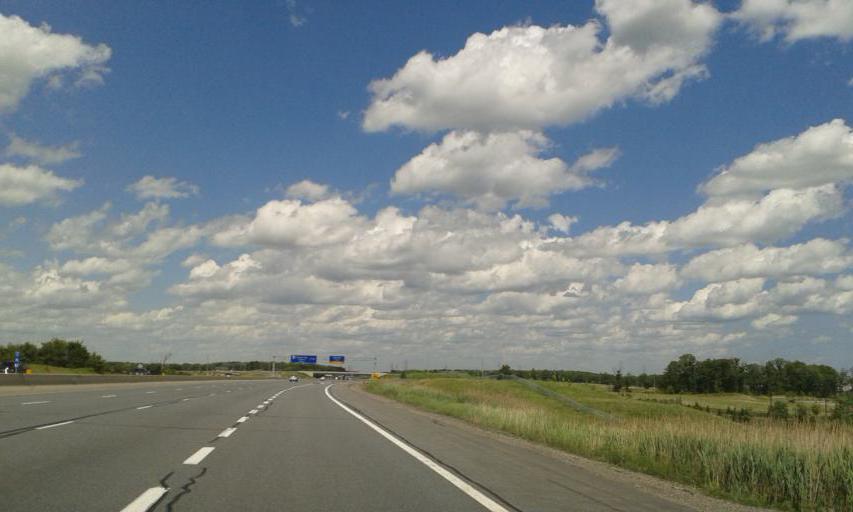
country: CA
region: Ontario
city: Burlington
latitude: 43.4091
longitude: -79.8269
